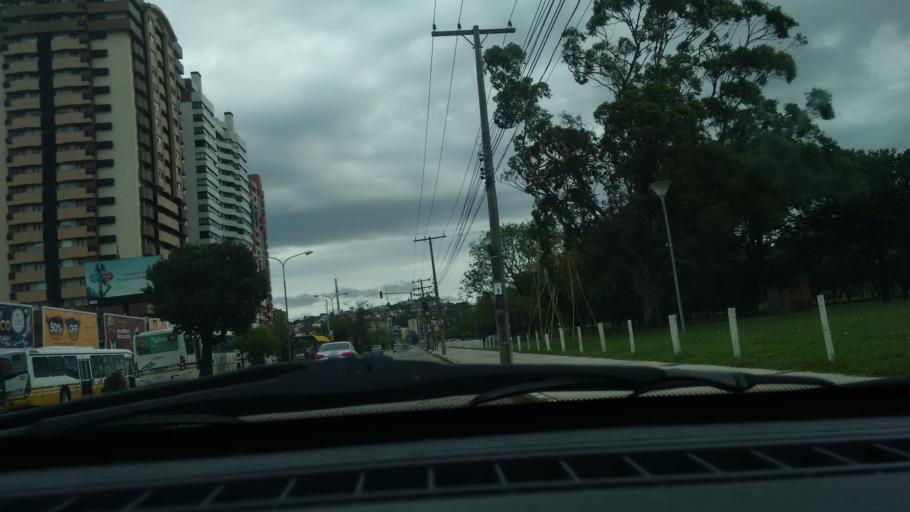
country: BR
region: Rio Grande do Sul
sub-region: Porto Alegre
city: Porto Alegre
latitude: -30.0540
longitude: -51.2302
